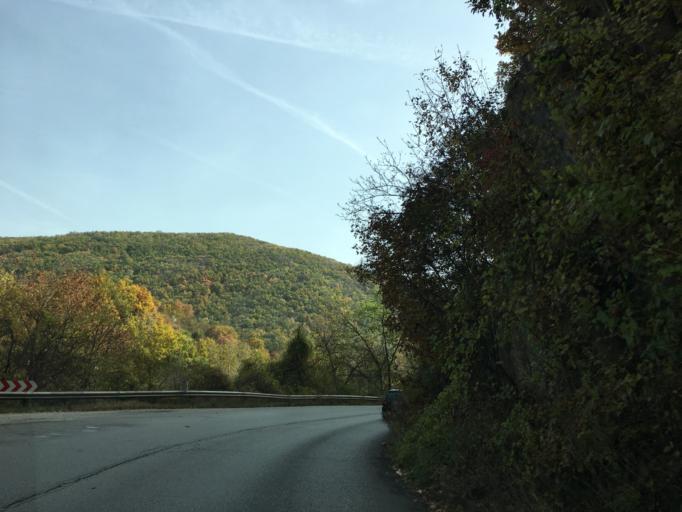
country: BG
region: Sofia-Capital
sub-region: Stolichna Obshtina
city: Sofia
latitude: 42.5555
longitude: 23.4244
